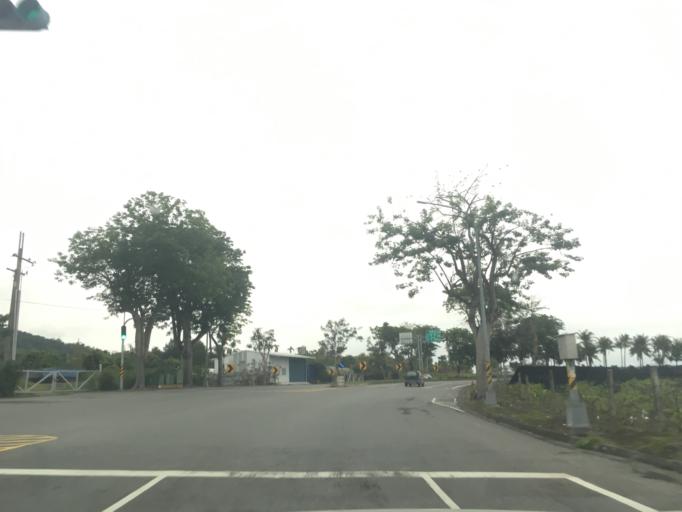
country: TW
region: Taiwan
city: Taitung City
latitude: 22.7126
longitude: 121.0452
